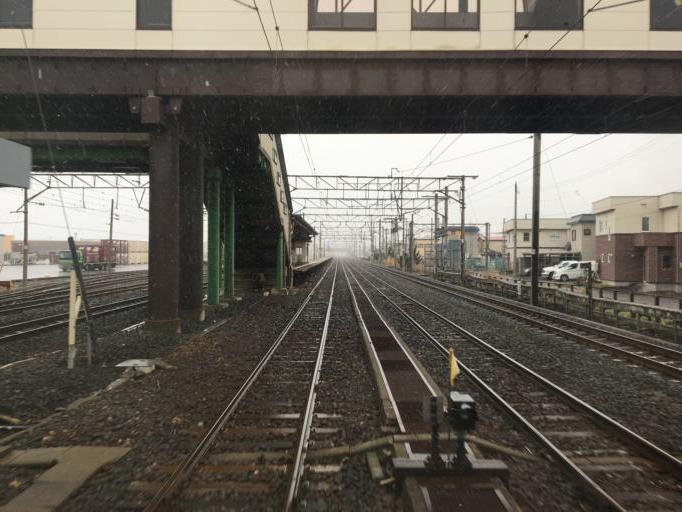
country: JP
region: Aomori
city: Aomori Shi
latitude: 40.8100
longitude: 140.7823
